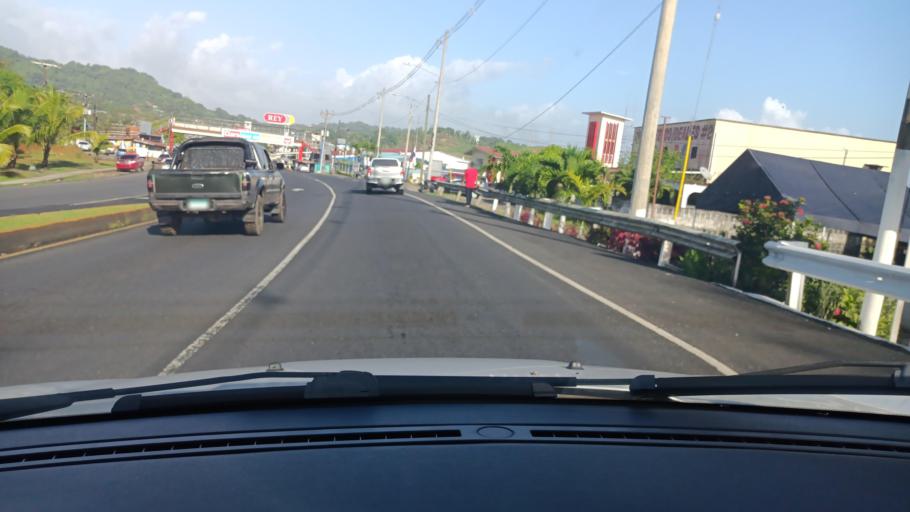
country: PA
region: Colon
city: Sabanitas
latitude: 9.3458
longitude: -79.8058
